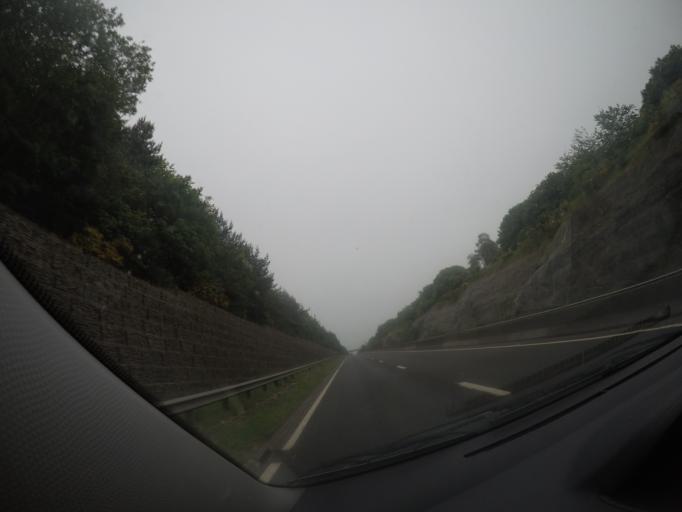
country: GB
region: Scotland
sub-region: Dundee City
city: Dundee
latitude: 56.5006
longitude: -2.9490
